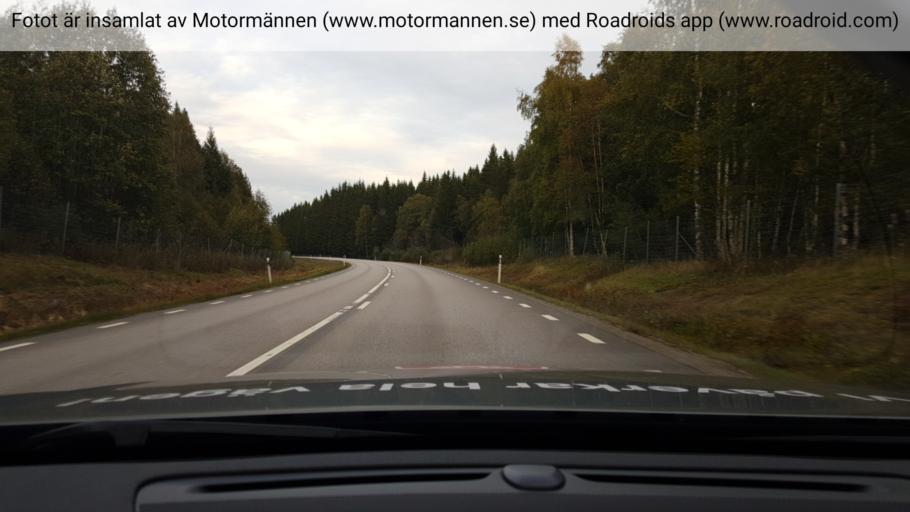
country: SE
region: Vaestra Goetaland
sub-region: Bengtsfors Kommun
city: Dals Langed
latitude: 59.0217
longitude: 12.3746
